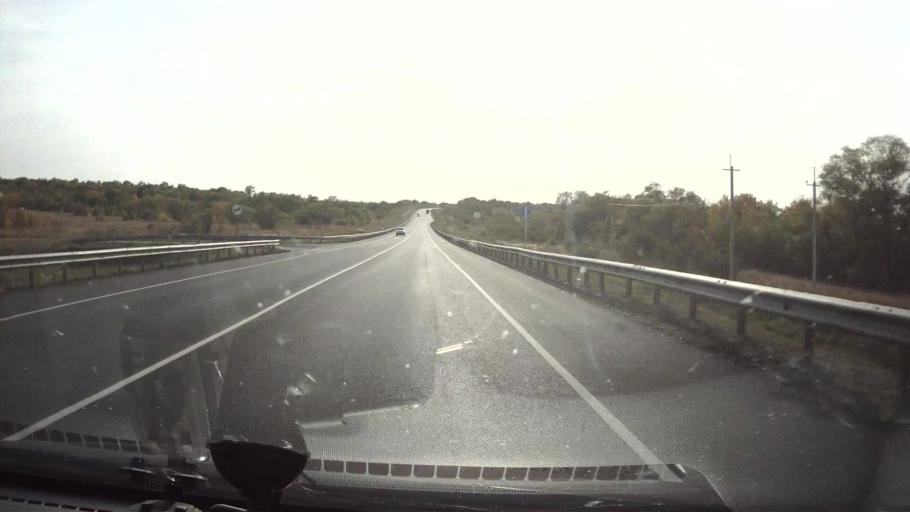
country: RU
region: Saratov
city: Shumeyka
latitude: 51.7841
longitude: 46.1317
